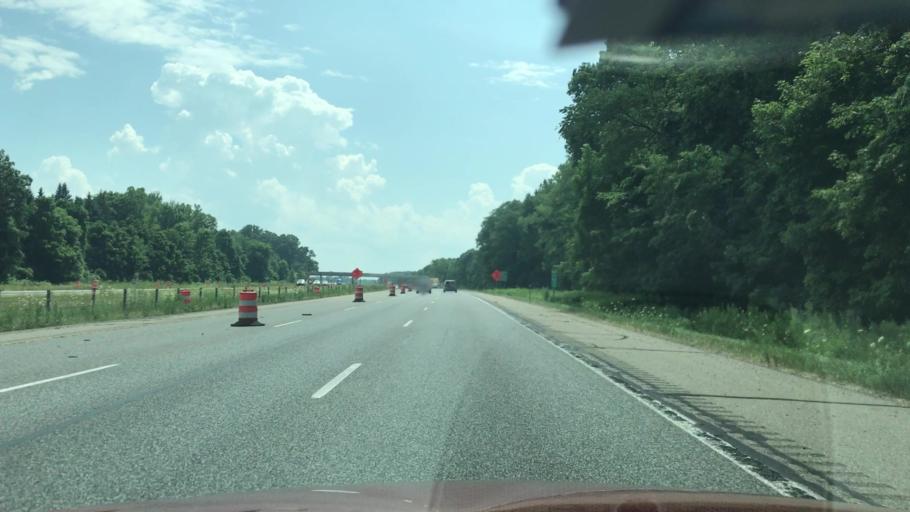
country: US
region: Michigan
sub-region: Berrien County
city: New Buffalo
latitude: 41.8175
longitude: -86.6915
